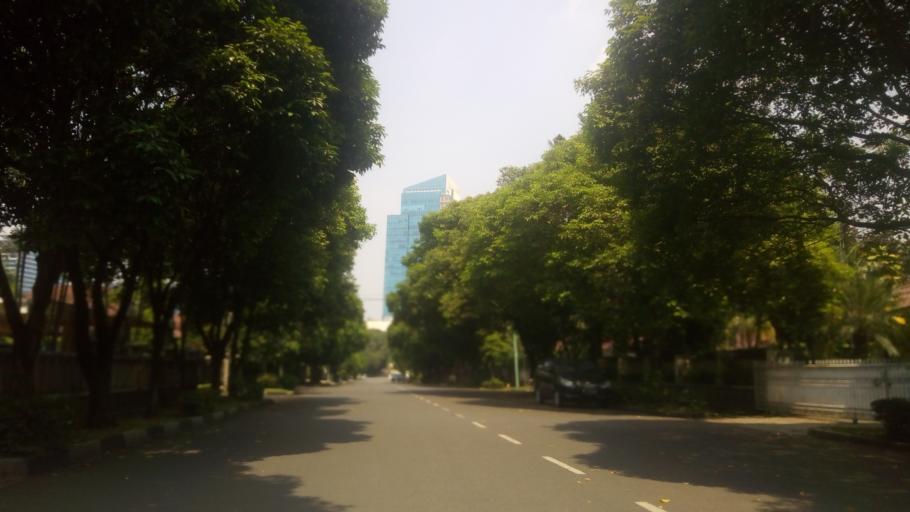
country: ID
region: Jakarta Raya
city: Jakarta
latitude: -6.2363
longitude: 106.8346
